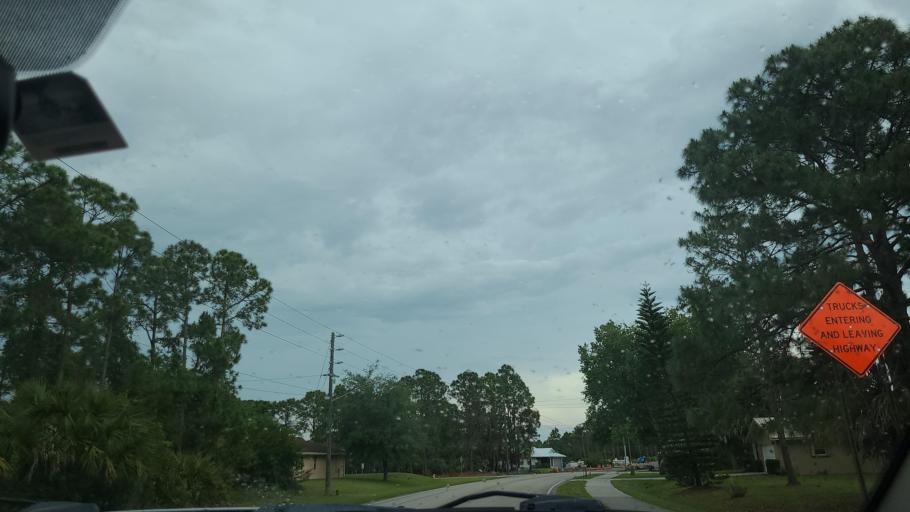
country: US
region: Florida
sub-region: Brevard County
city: June Park
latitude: 27.9662
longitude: -80.6775
